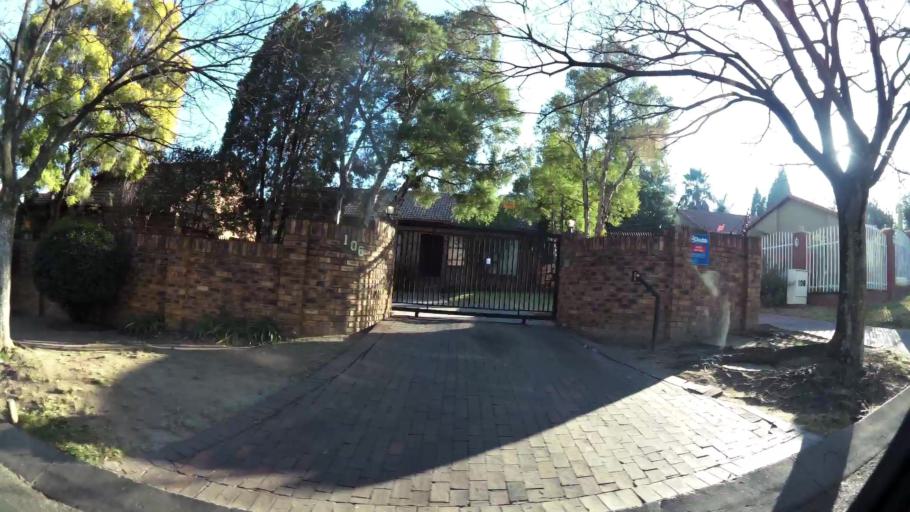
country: ZA
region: Gauteng
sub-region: City of Johannesburg Metropolitan Municipality
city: Midrand
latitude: -26.0354
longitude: 28.0758
